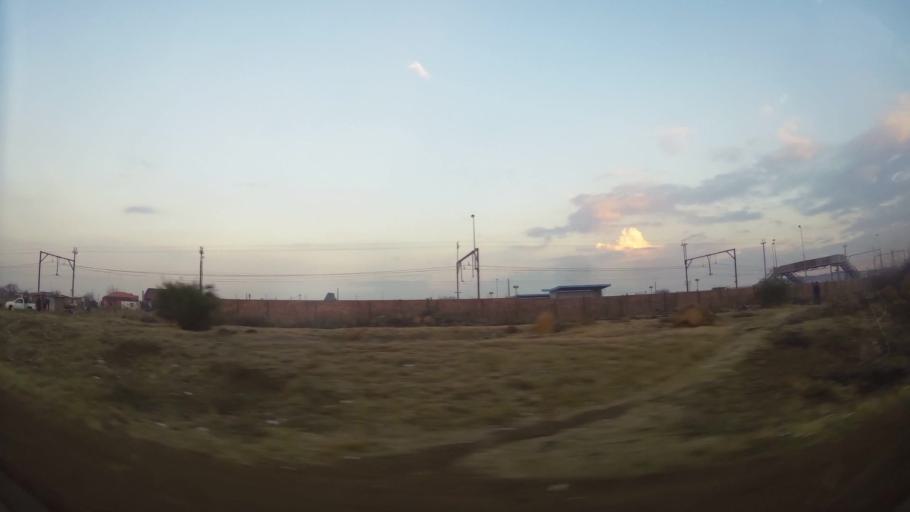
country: ZA
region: Gauteng
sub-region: City of Johannesburg Metropolitan Municipality
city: Orange Farm
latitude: -26.5565
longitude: 27.8787
